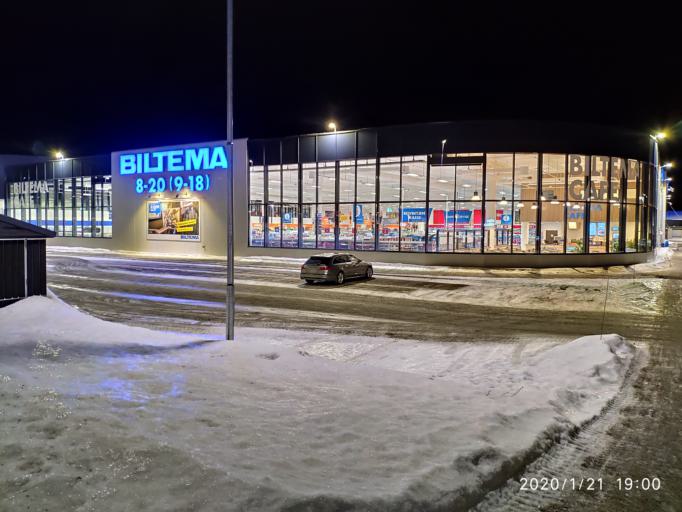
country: NO
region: Oppland
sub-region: Nord-Fron
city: Vinstra
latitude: 61.5945
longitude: 9.7285
